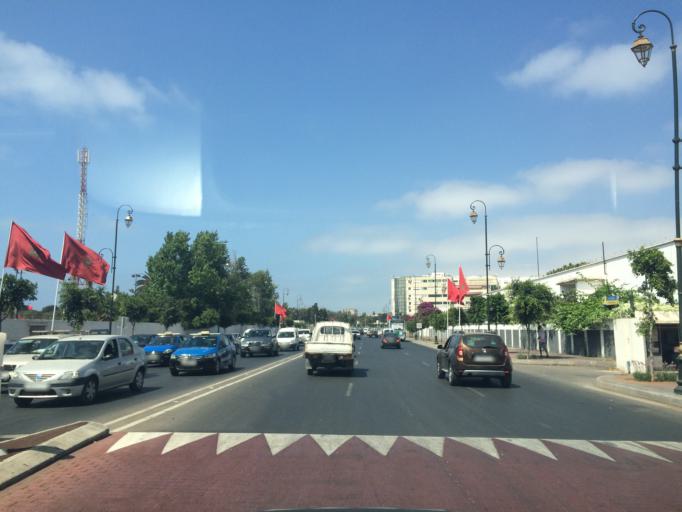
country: MA
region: Rabat-Sale-Zemmour-Zaer
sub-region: Rabat
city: Rabat
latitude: 34.0013
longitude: -6.8599
